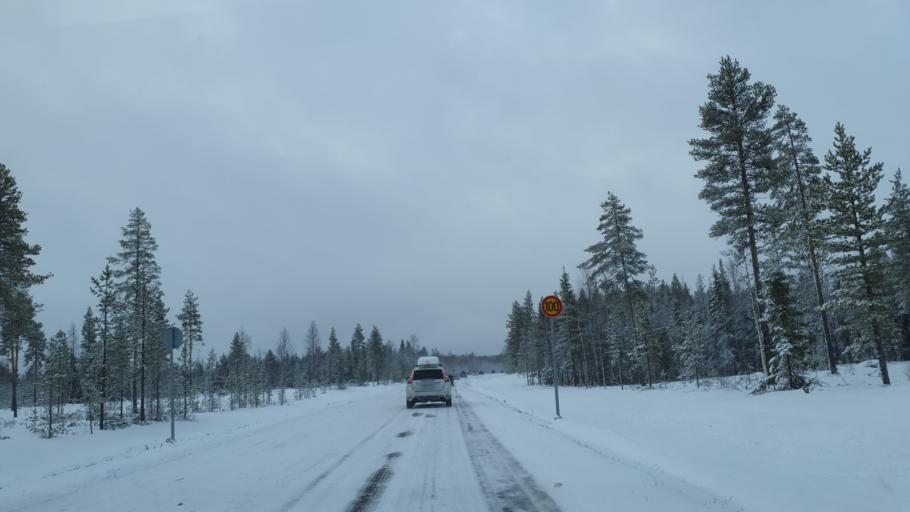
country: FI
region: Lapland
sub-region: Tunturi-Lappi
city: Kittilae
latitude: 67.3938
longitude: 24.9135
